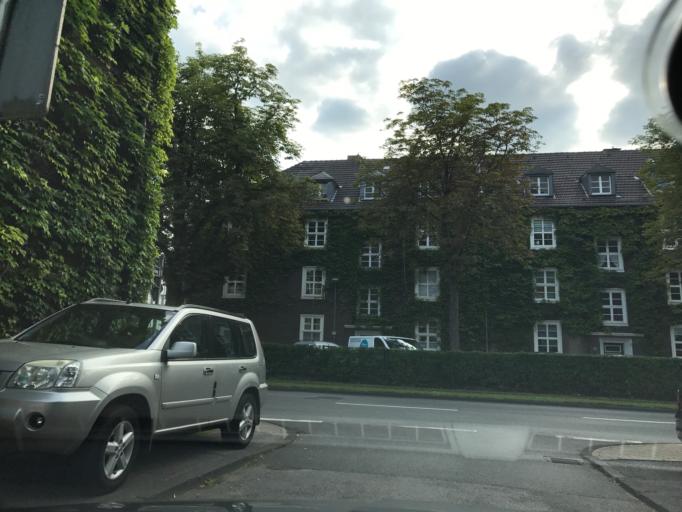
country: DE
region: North Rhine-Westphalia
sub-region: Regierungsbezirk Dusseldorf
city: Essen
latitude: 51.4295
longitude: 6.9742
